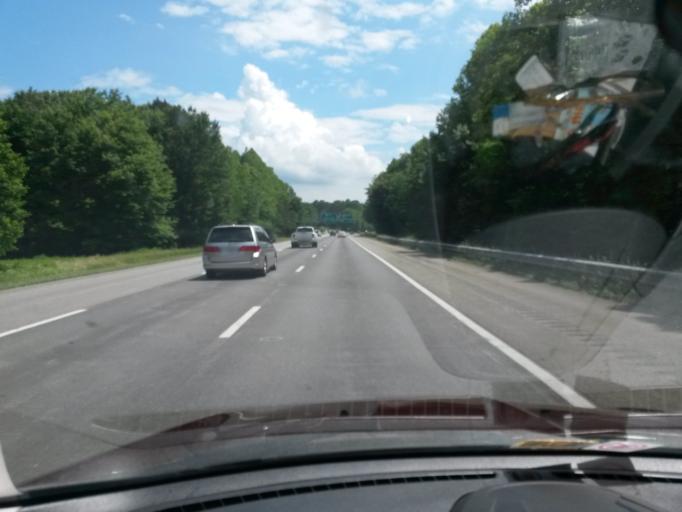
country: US
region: North Carolina
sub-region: Surry County
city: Dobson
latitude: 36.5002
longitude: -80.7425
